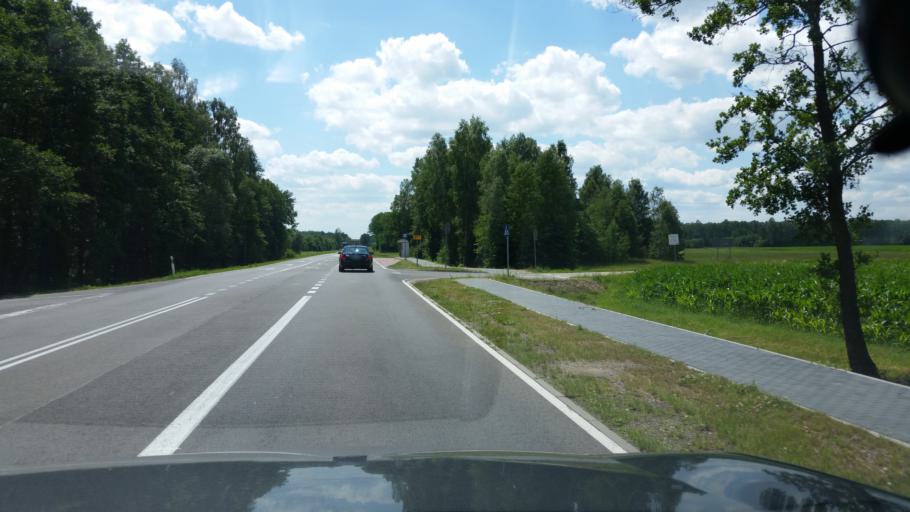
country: PL
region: Masovian Voivodeship
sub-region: Powiat ostrowski
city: Ostrow Mazowiecka
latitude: 52.9133
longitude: 21.8753
